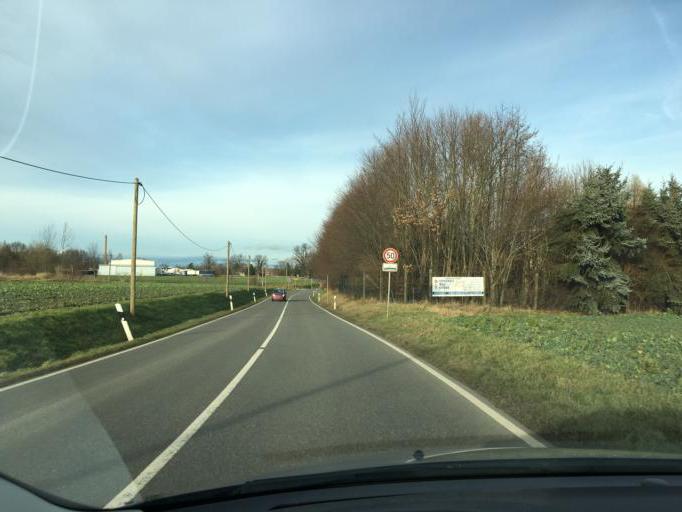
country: DE
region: Thuringia
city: Nobitz
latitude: 50.9964
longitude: 12.4736
